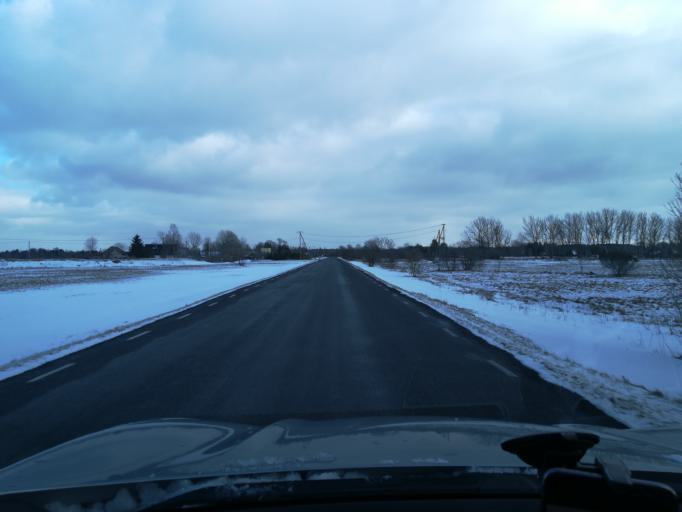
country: EE
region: Harju
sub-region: Harku vald
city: Tabasalu
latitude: 59.4289
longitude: 24.4111
